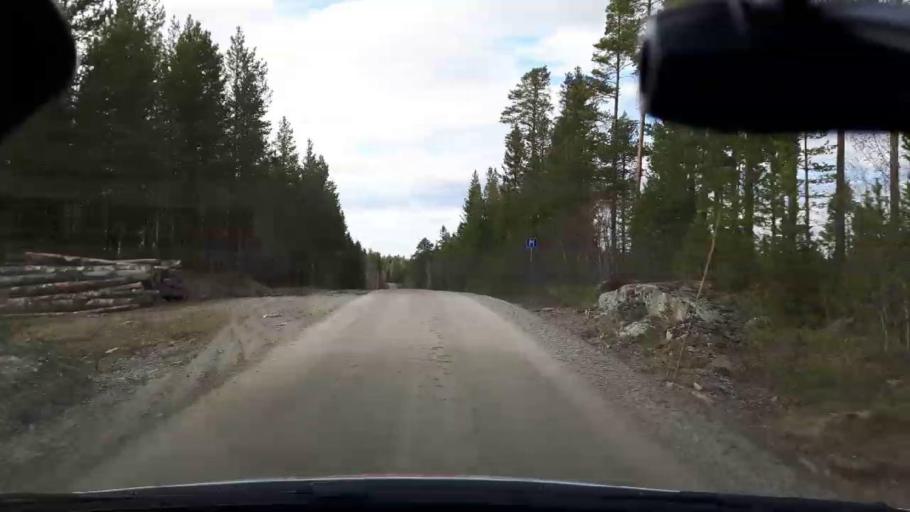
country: SE
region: Jaemtland
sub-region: Bergs Kommun
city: Hoverberg
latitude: 62.8875
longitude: 14.6585
